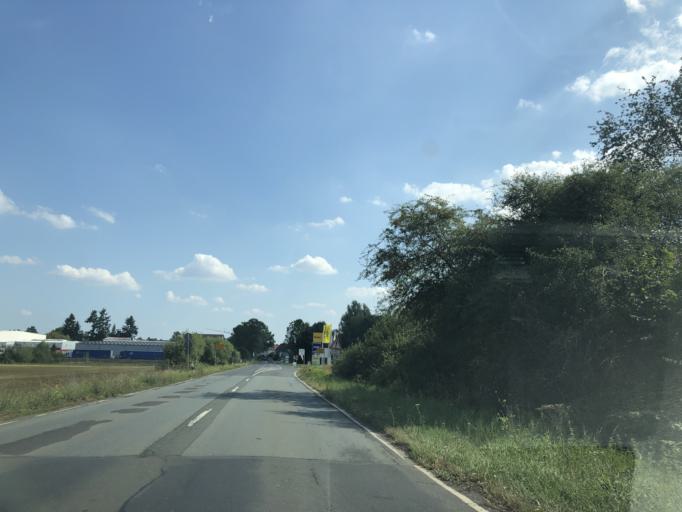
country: DE
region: Hesse
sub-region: Regierungsbezirk Giessen
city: Kirchhain
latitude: 50.8294
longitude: 8.9084
